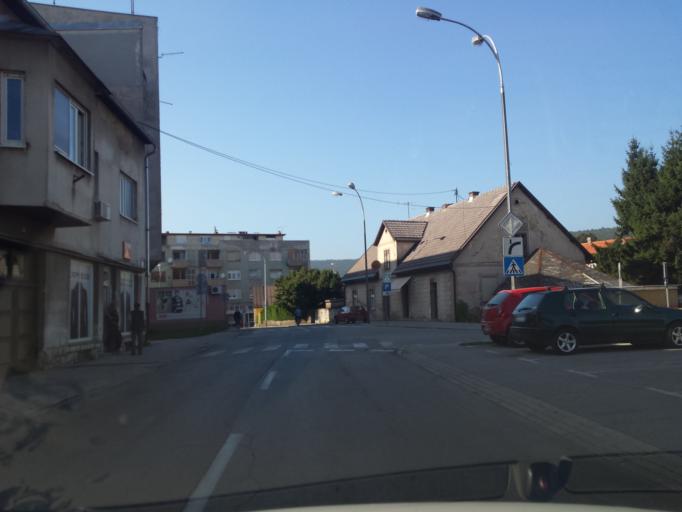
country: HR
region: Karlovacka
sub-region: Grad Ogulin
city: Ogulin
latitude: 45.2657
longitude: 15.2293
